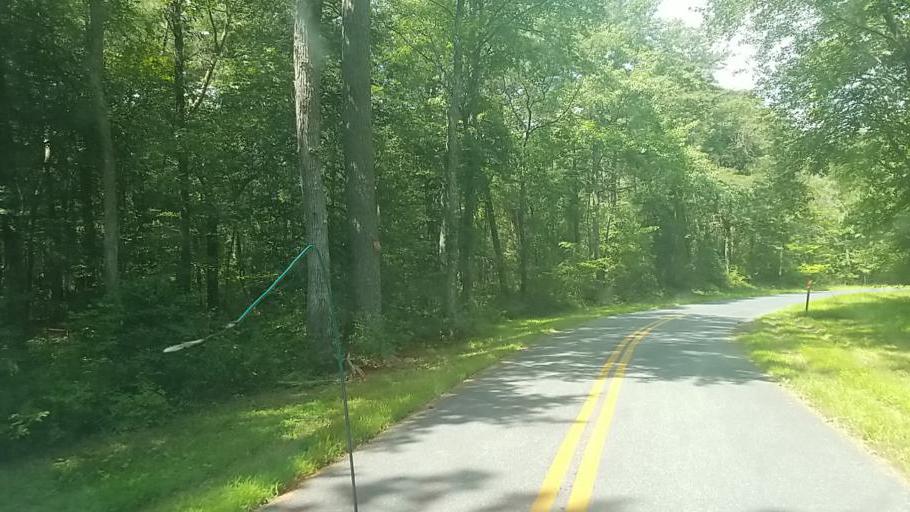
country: US
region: Maryland
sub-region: Wicomico County
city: Pittsville
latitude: 38.2849
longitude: -75.4776
